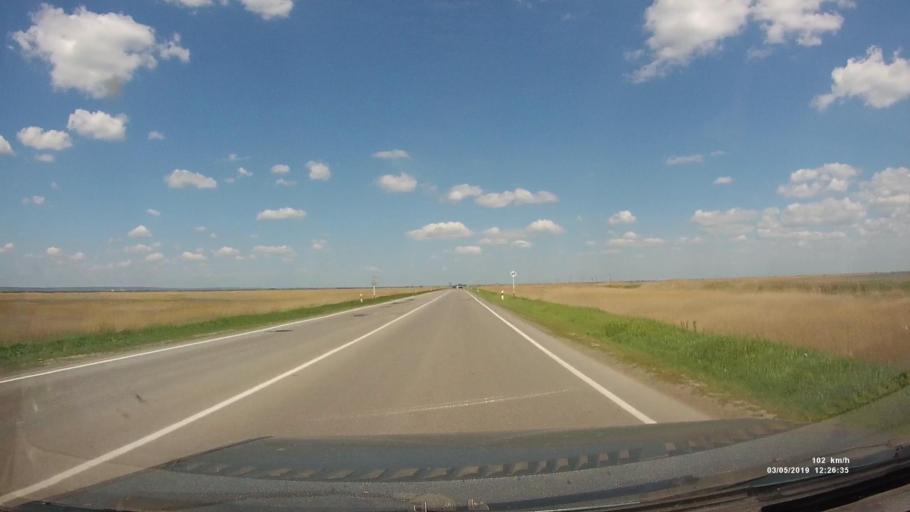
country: RU
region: Rostov
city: Semikarakorsk
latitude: 47.4473
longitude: 40.7148
